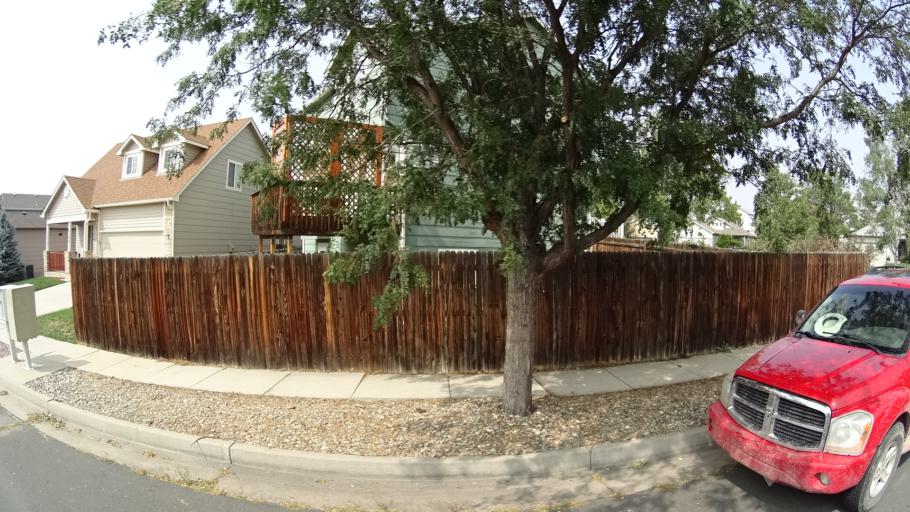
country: US
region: Colorado
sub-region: El Paso County
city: Cimarron Hills
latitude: 38.9231
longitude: -104.7266
